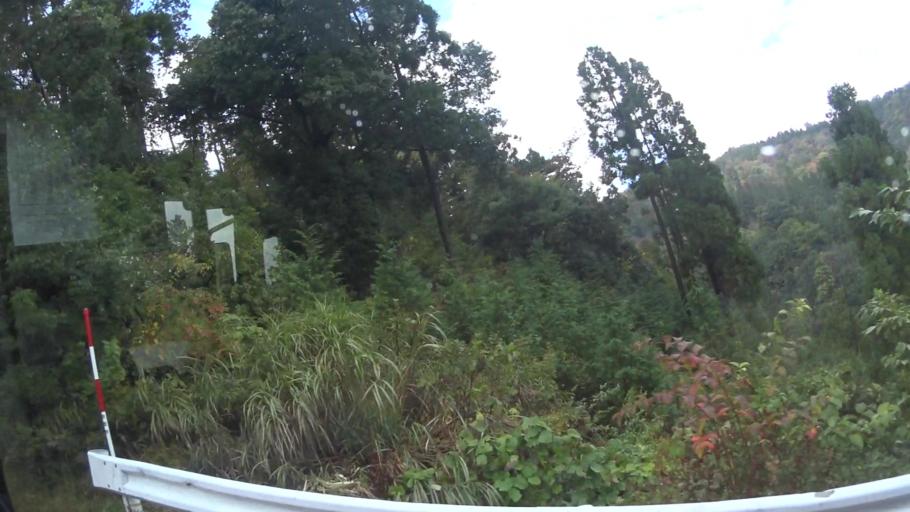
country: JP
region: Kyoto
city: Miyazu
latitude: 35.5926
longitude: 135.1876
